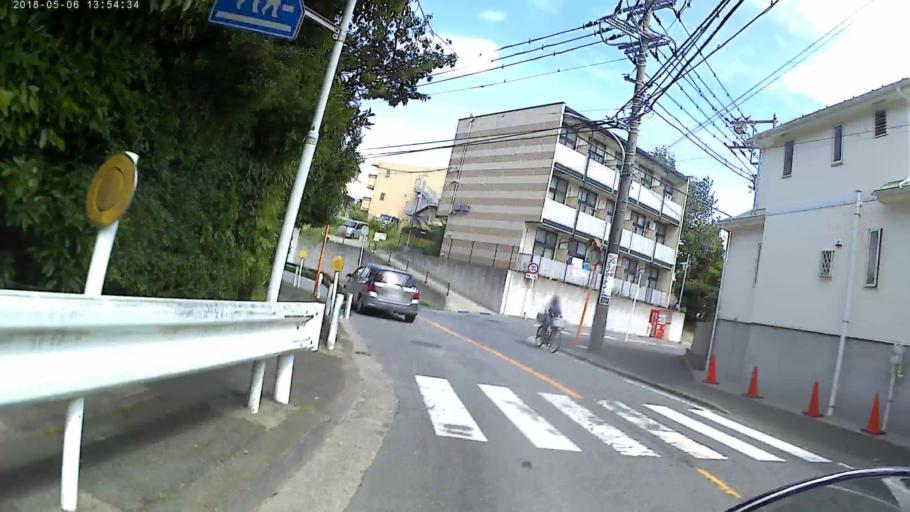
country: JP
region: Kanagawa
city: Yokohama
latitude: 35.4334
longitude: 139.5799
